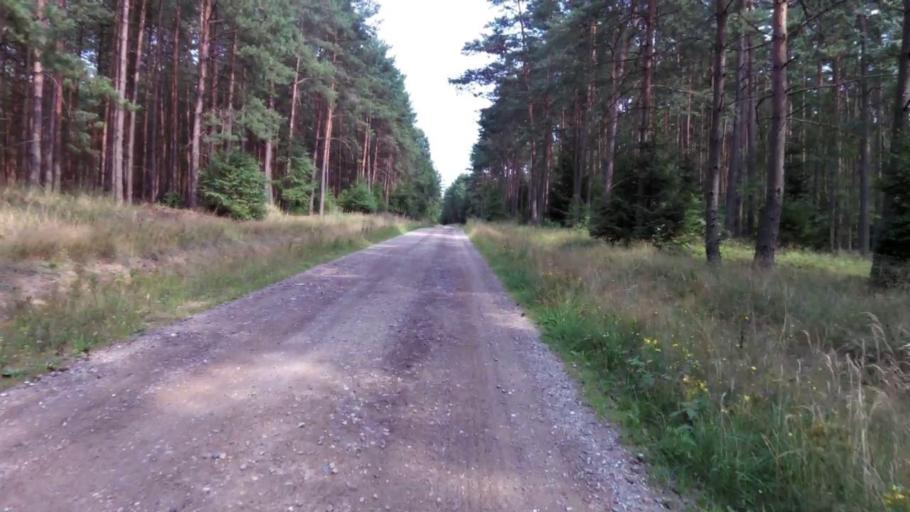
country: PL
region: West Pomeranian Voivodeship
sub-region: Powiat drawski
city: Zlocieniec
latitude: 53.5619
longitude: 15.9323
